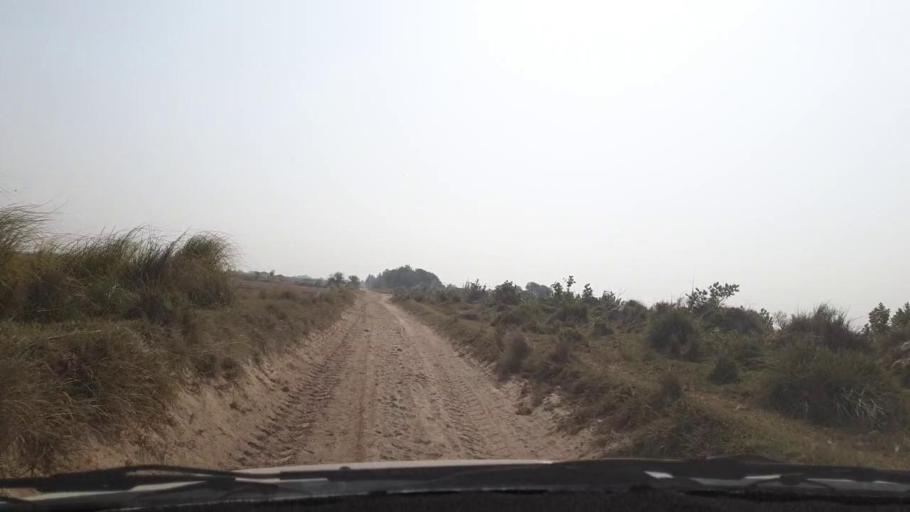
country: PK
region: Sindh
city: Tando Muhammad Khan
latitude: 25.0733
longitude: 68.3636
